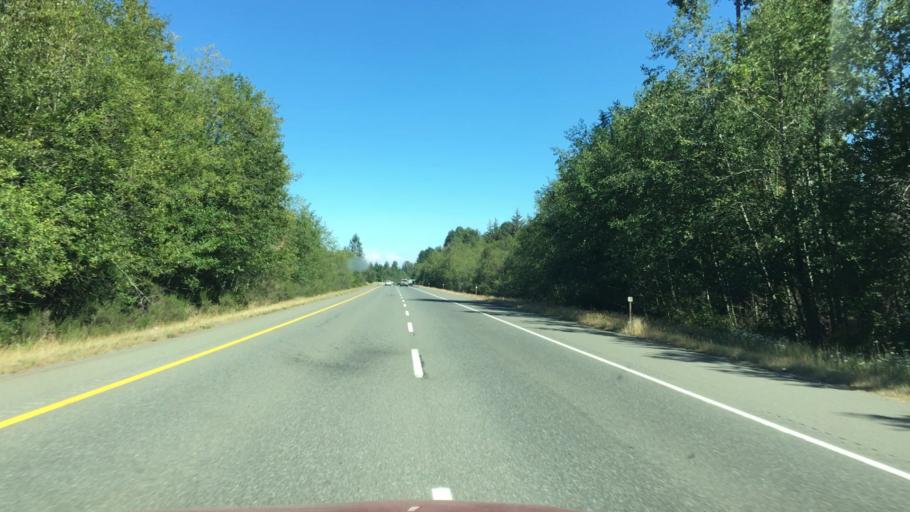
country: CA
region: British Columbia
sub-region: Regional District of Nanaimo
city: Parksville
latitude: 49.3168
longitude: -124.3804
